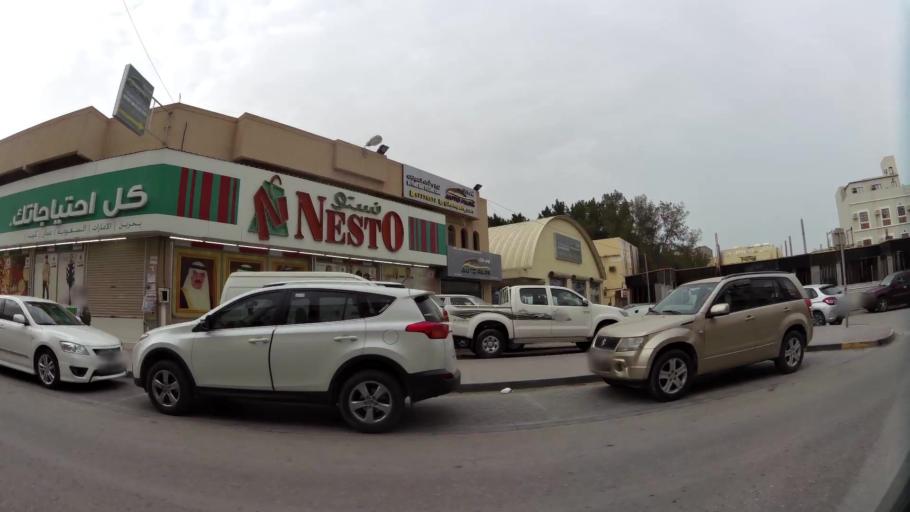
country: BH
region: Northern
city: Ar Rifa'
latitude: 26.1167
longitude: 50.5715
